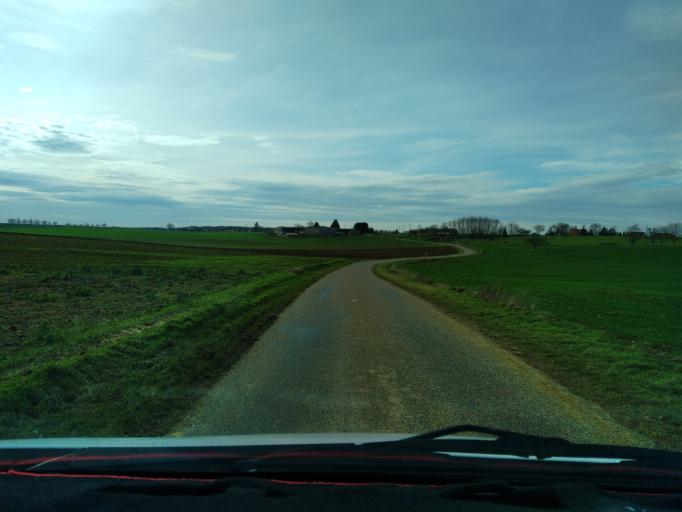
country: FR
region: Franche-Comte
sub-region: Departement de la Haute-Saone
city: Marnay
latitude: 47.3616
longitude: 5.6878
